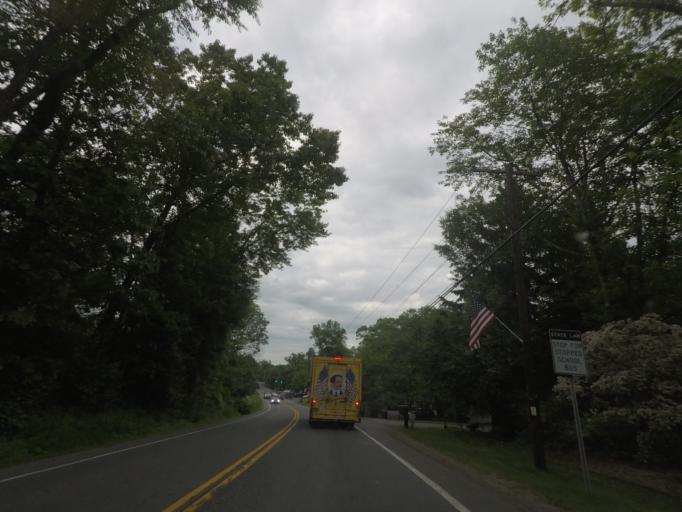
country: US
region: New York
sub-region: Orange County
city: Gardnertown
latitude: 41.5308
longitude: -74.0659
